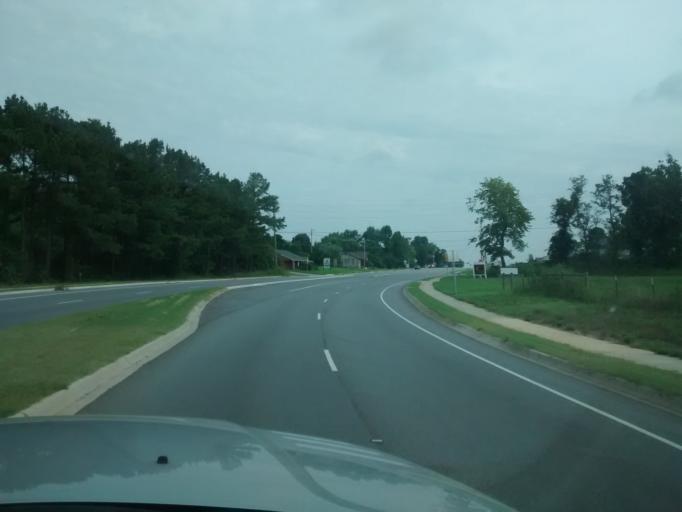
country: US
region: Arkansas
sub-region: Washington County
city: Springdale
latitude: 36.1475
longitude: -94.1188
